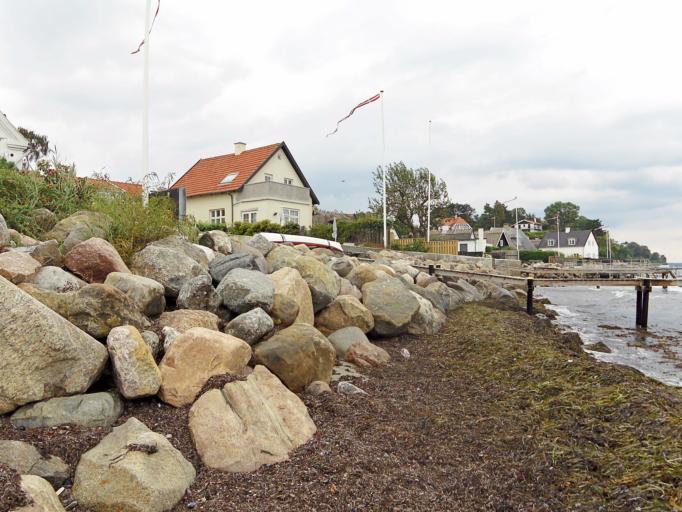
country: DK
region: Capital Region
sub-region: Fredensborg Kommune
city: Humlebaek
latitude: 55.9542
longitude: 12.5357
